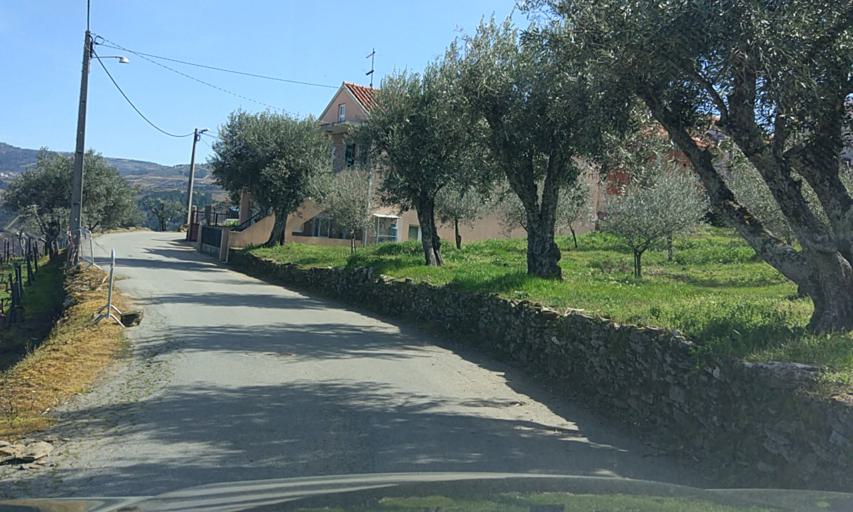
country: PT
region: Vila Real
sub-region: Sabrosa
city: Sabrosa
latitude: 41.3075
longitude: -7.5600
